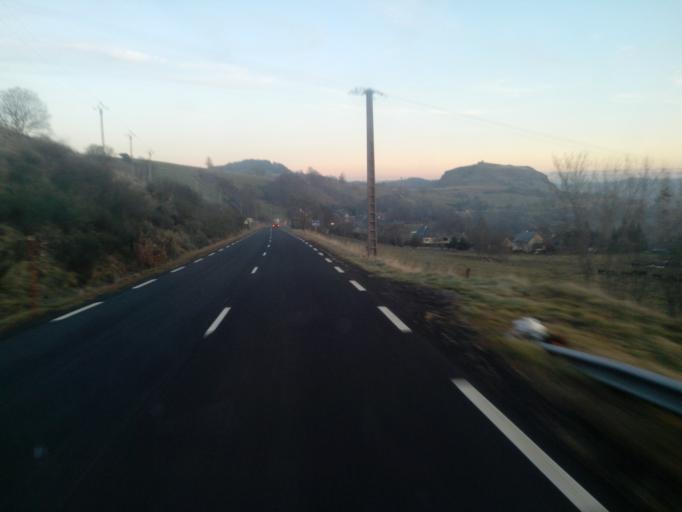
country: FR
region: Auvergne
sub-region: Departement du Cantal
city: Murat
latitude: 45.1327
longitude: 2.8365
